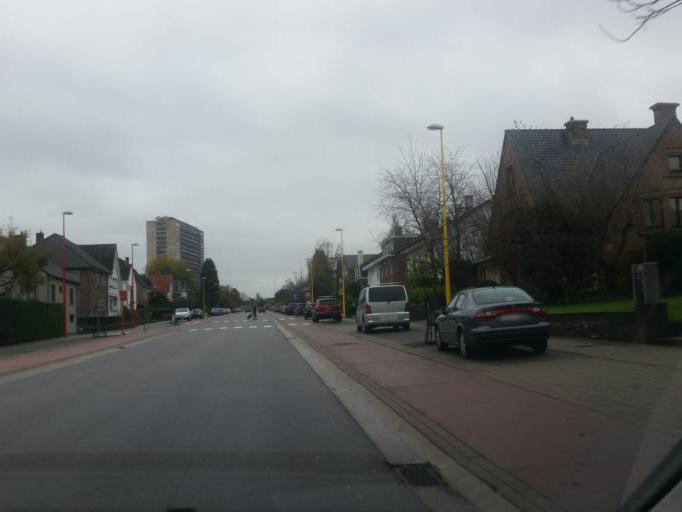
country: BE
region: Flanders
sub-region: Provincie Vlaams-Brabant
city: Grimbergen
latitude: 50.9051
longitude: 4.3569
